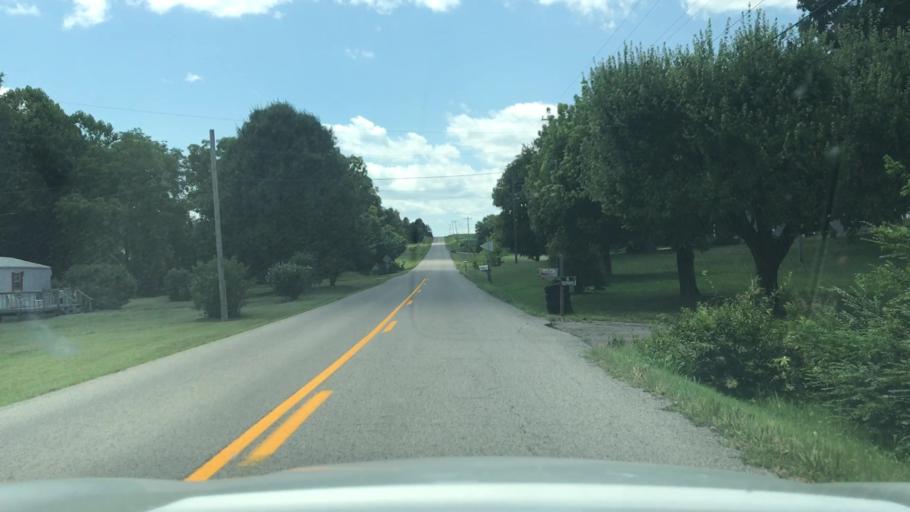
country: US
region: Kentucky
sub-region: Christian County
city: Hopkinsville
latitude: 36.9710
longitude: -87.3737
